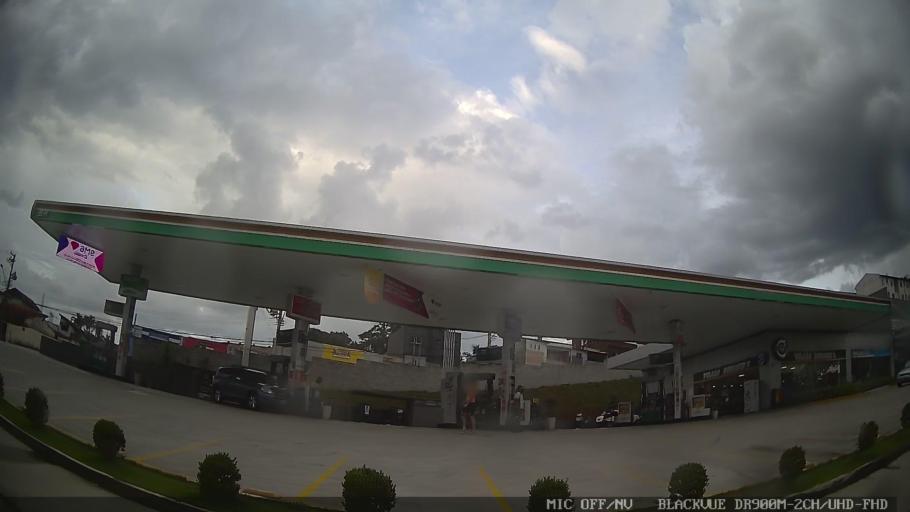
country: BR
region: Sao Paulo
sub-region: Mogi das Cruzes
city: Mogi das Cruzes
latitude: -23.5512
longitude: -46.1836
